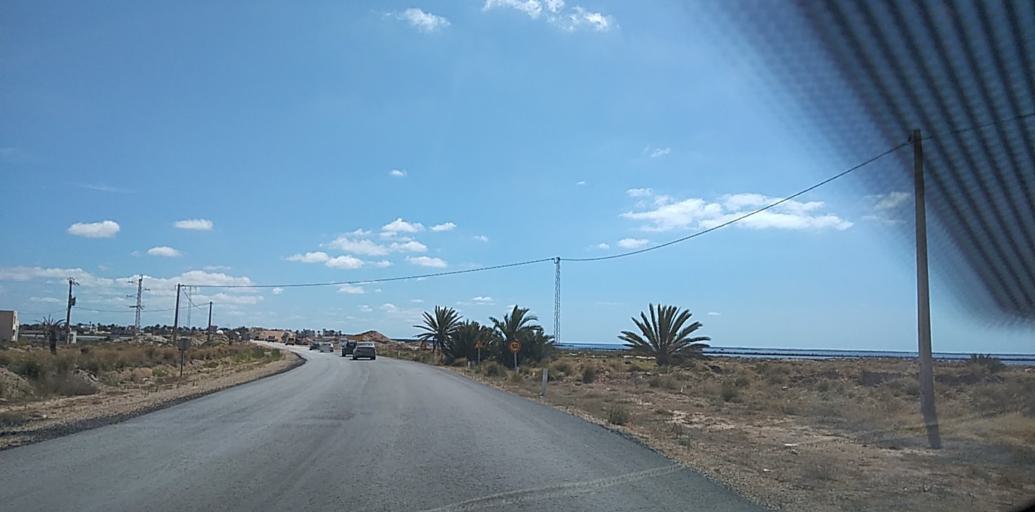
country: TN
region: Safaqis
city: Al Qarmadah
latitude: 34.6604
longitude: 11.1196
